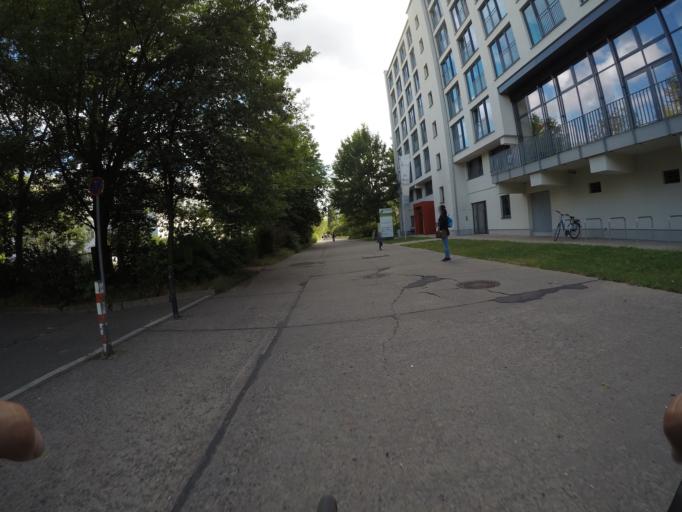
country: DE
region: Berlin
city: Marzahn
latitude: 52.5467
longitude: 13.5497
